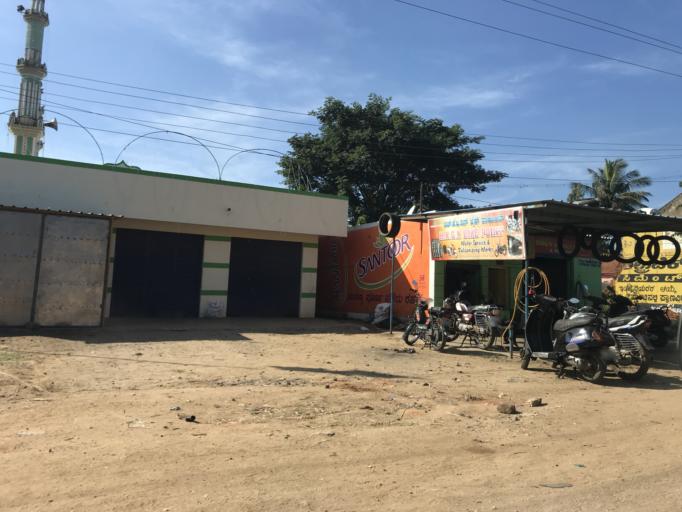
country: IN
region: Karnataka
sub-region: Mysore
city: Sargur
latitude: 12.1216
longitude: 76.4818
